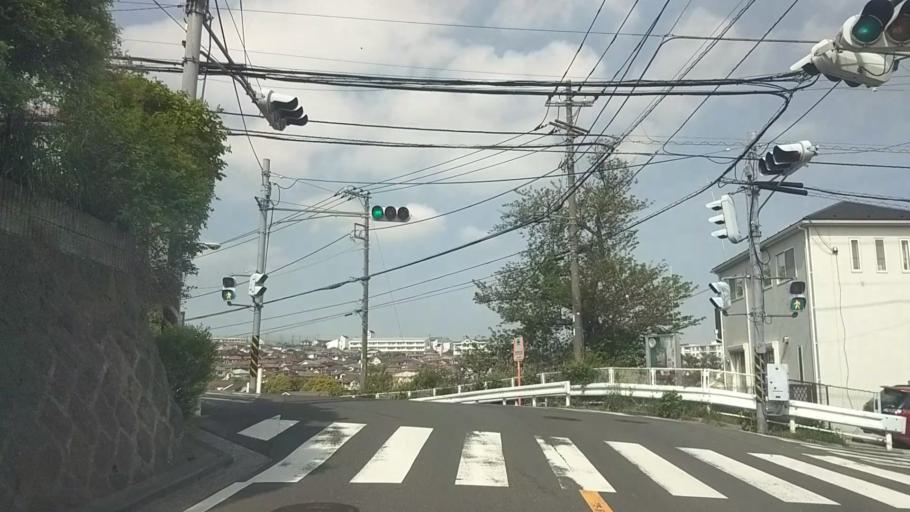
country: JP
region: Kanagawa
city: Yokohama
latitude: 35.3713
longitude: 139.6258
